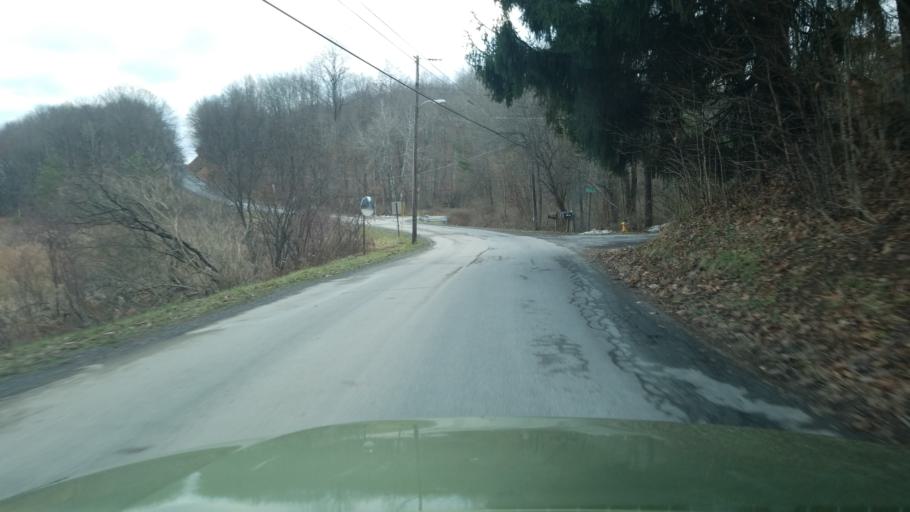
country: US
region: Pennsylvania
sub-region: Jefferson County
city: Falls Creek
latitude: 41.1363
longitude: -78.7892
